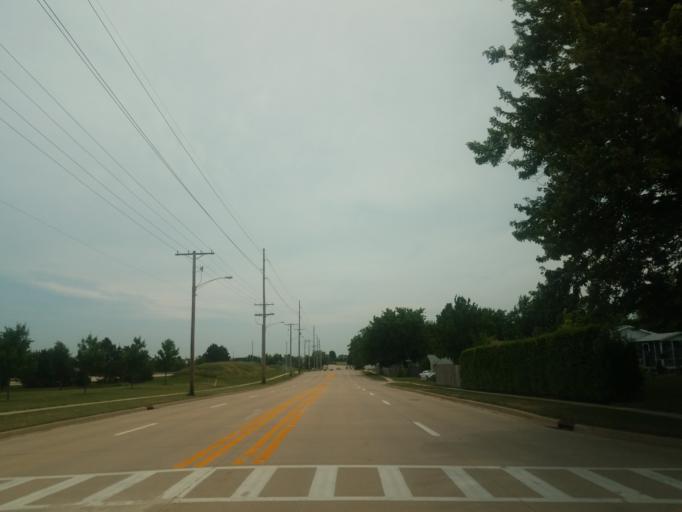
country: US
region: Illinois
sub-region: McLean County
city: Normal
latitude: 40.5214
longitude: -88.9437
